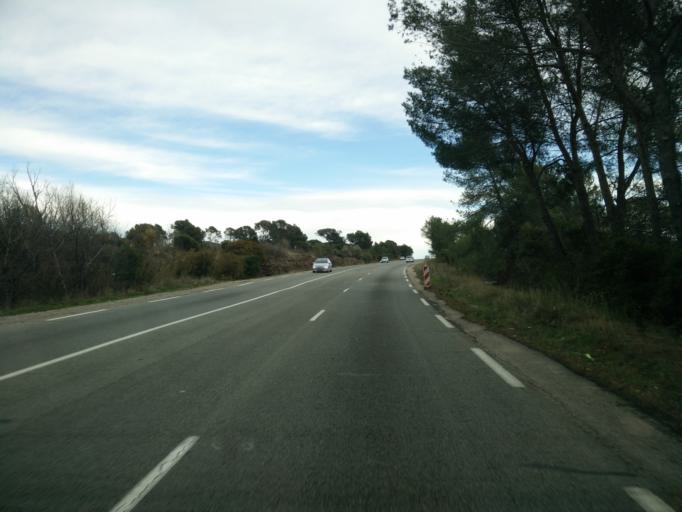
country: FR
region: Provence-Alpes-Cote d'Azur
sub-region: Departement du Var
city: Roquebrune-sur-Argens
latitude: 43.4657
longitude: 6.6186
